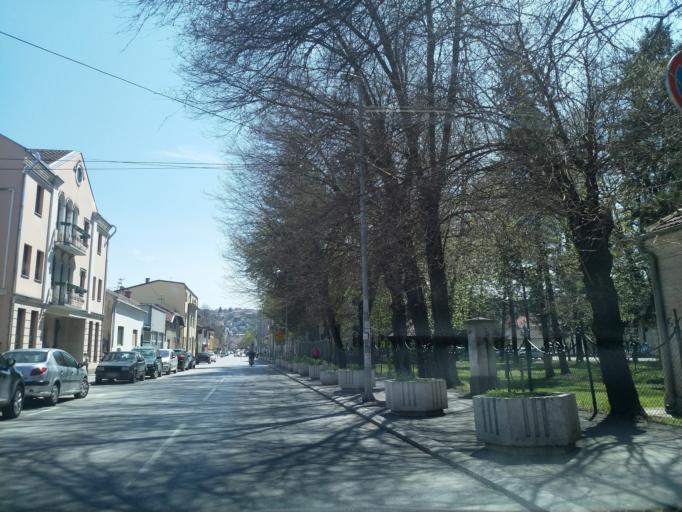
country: RS
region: Central Serbia
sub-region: Kolubarski Okrug
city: Valjevo
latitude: 44.2737
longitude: 19.8838
